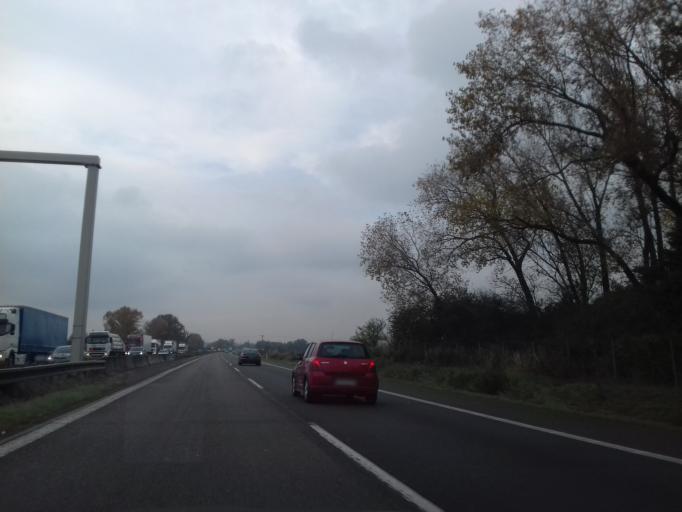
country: SK
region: Bratislavsky
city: Stupava
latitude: 48.2233
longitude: 17.0272
